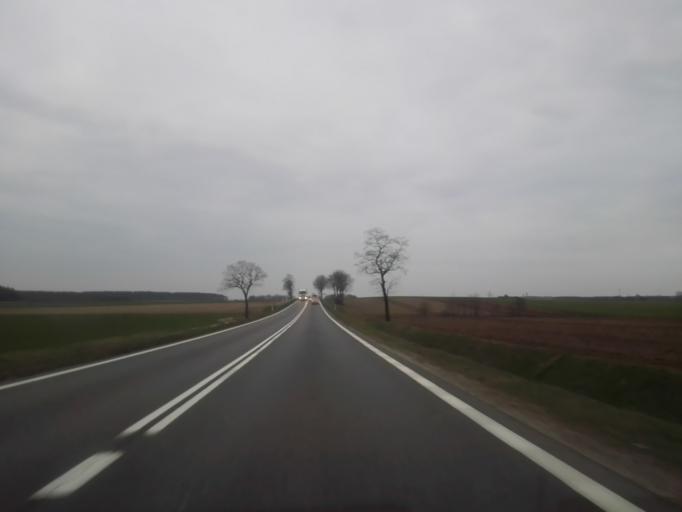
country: PL
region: Podlasie
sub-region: Powiat kolnenski
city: Stawiski
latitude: 53.4266
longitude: 22.1692
